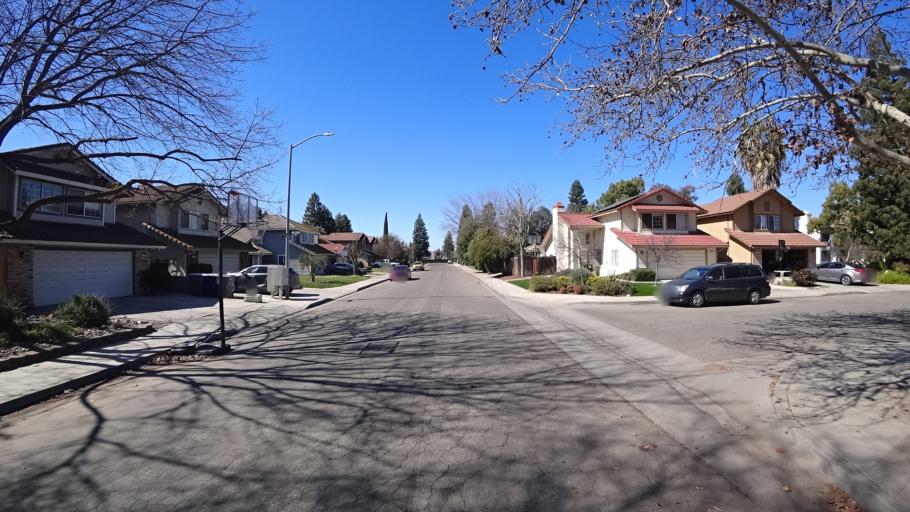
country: US
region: California
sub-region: Fresno County
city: Clovis
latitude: 36.8487
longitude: -119.7625
